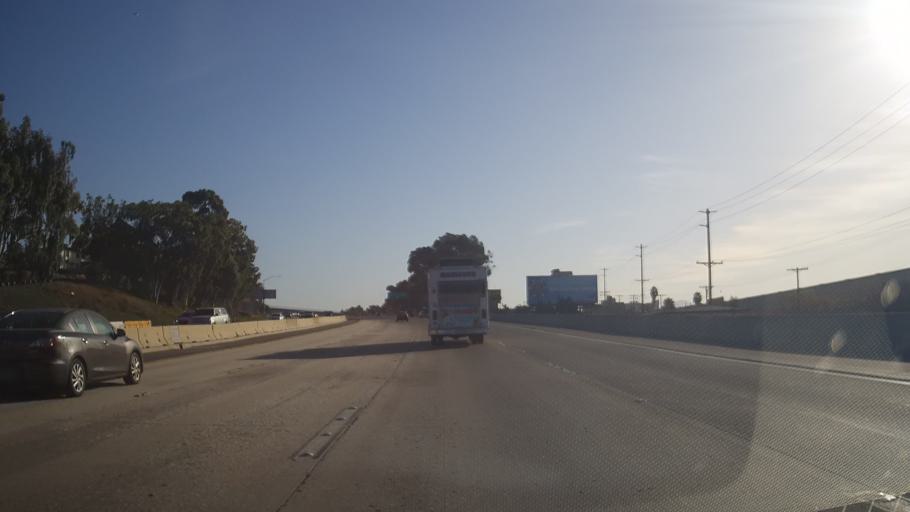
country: US
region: California
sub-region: San Diego County
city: Lemon Grove
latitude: 32.7446
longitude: -117.0375
